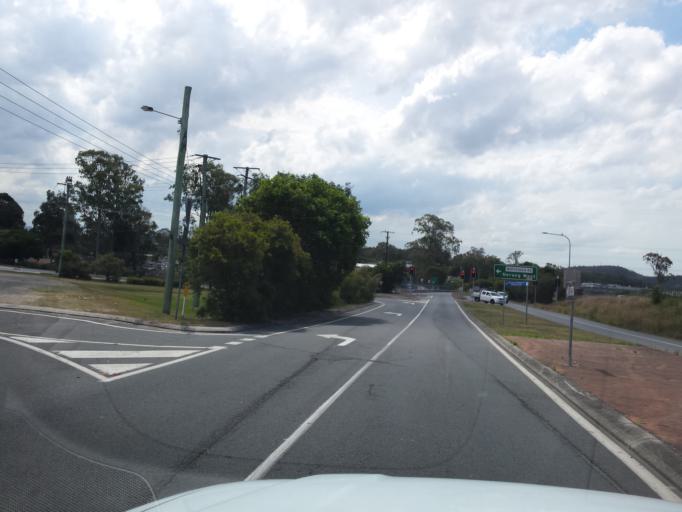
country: AU
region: Queensland
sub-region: Gold Coast
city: Nerang
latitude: -28.0065
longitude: 153.3416
